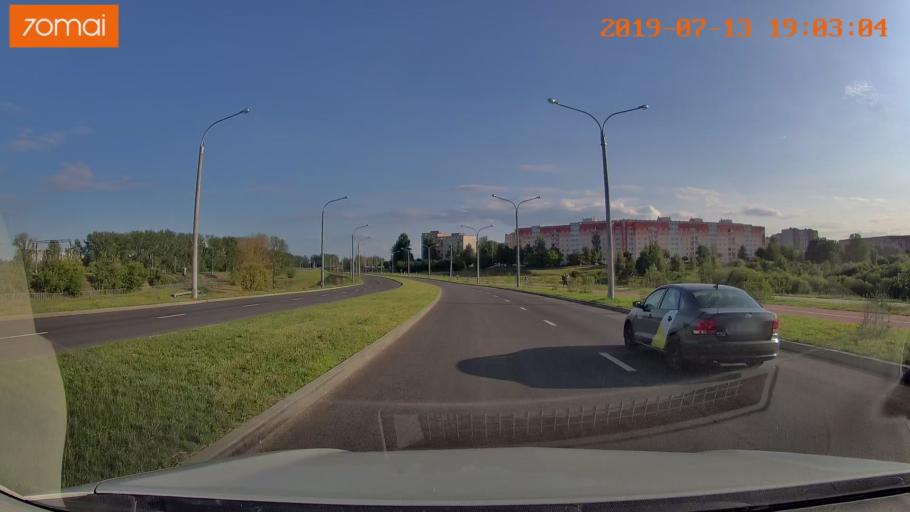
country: BY
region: Minsk
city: Syenitsa
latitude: 53.8568
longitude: 27.5564
